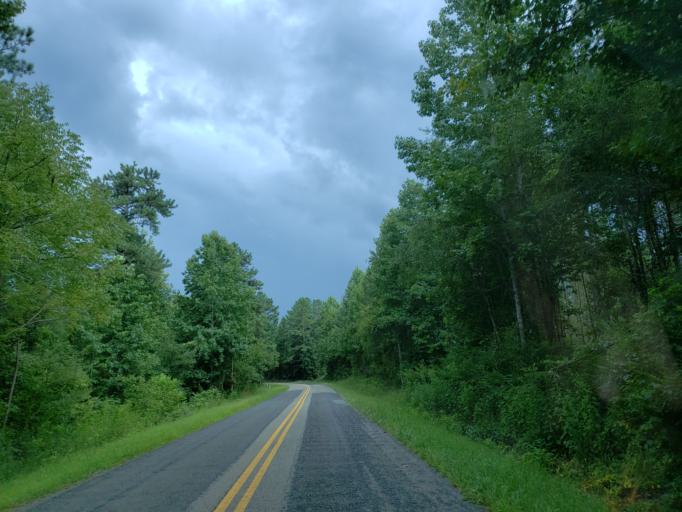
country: US
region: Georgia
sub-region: Pickens County
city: Jasper
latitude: 34.3910
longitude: -84.4662
